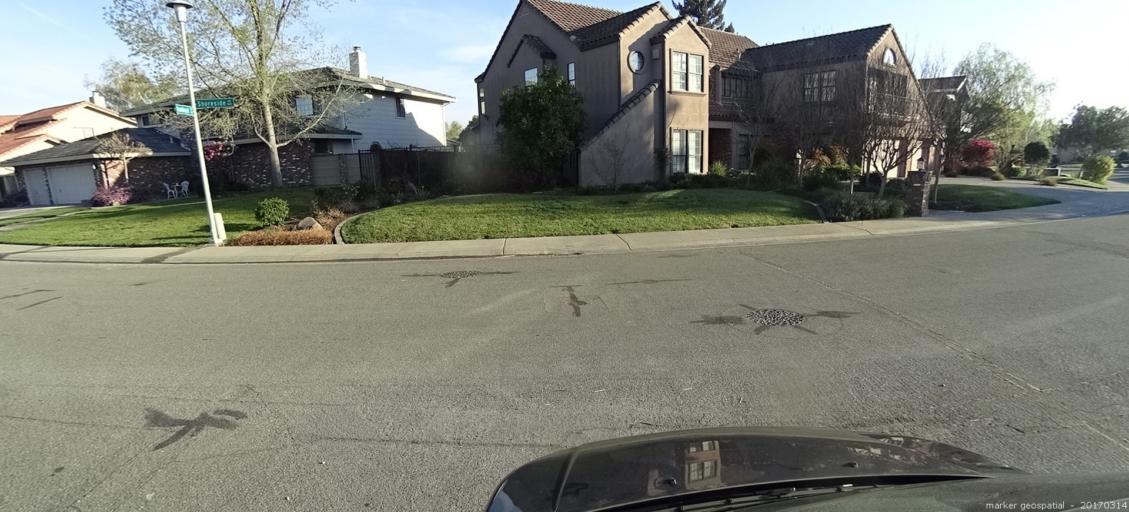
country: US
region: California
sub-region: Yolo County
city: West Sacramento
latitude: 38.5098
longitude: -121.5386
